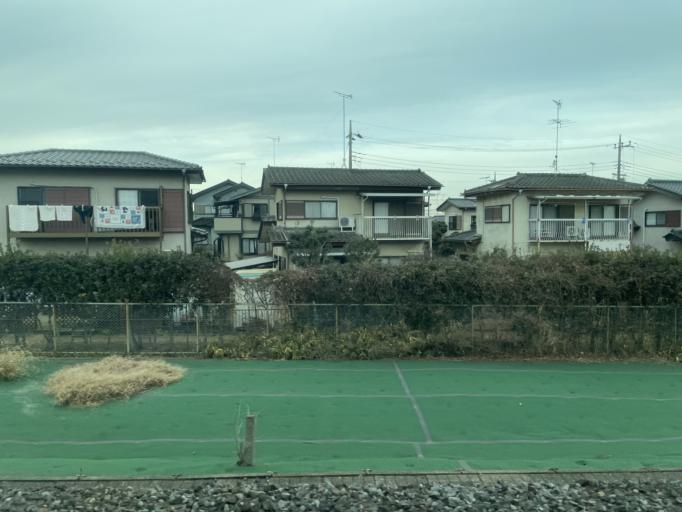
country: JP
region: Ibaraki
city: Koga
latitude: 36.1583
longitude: 139.7156
